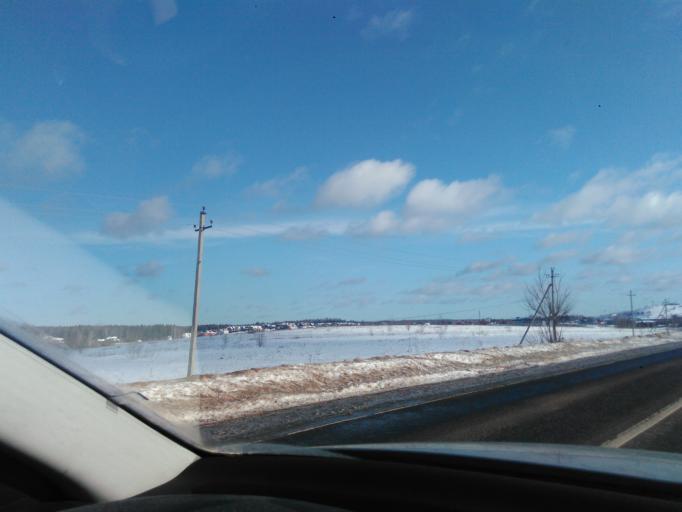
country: RU
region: Moskovskaya
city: Dedenevo
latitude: 56.2785
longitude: 37.5416
